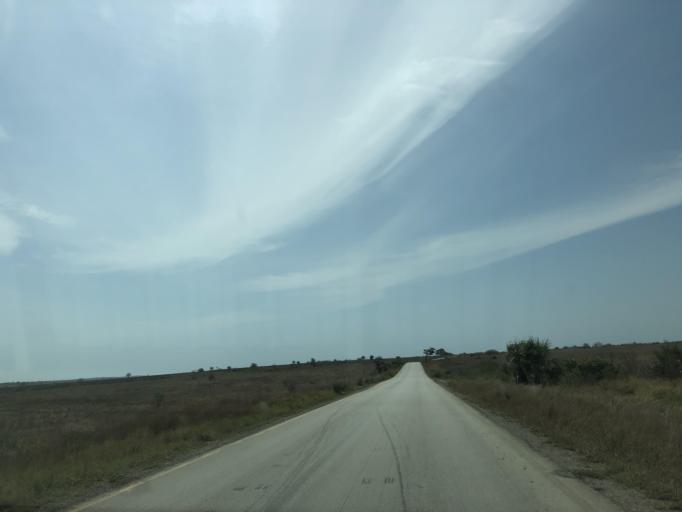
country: AO
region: Cuanza Sul
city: Sumbe
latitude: -10.3606
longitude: 13.6434
